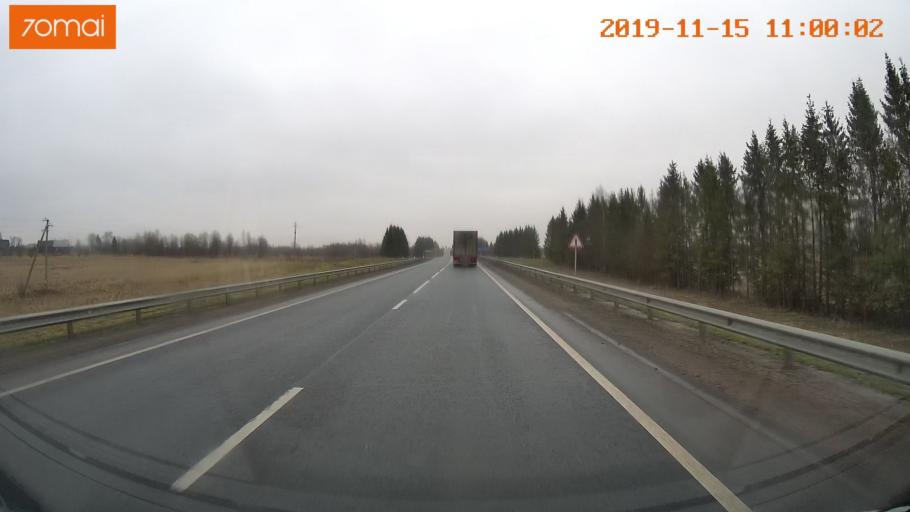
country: RU
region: Vologda
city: Chebsara
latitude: 59.1393
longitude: 38.8892
